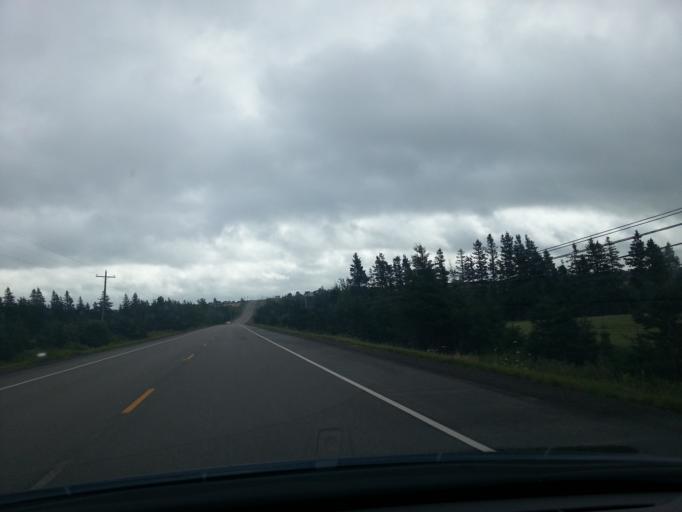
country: CA
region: Prince Edward Island
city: Montague
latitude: 46.4140
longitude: -62.6329
